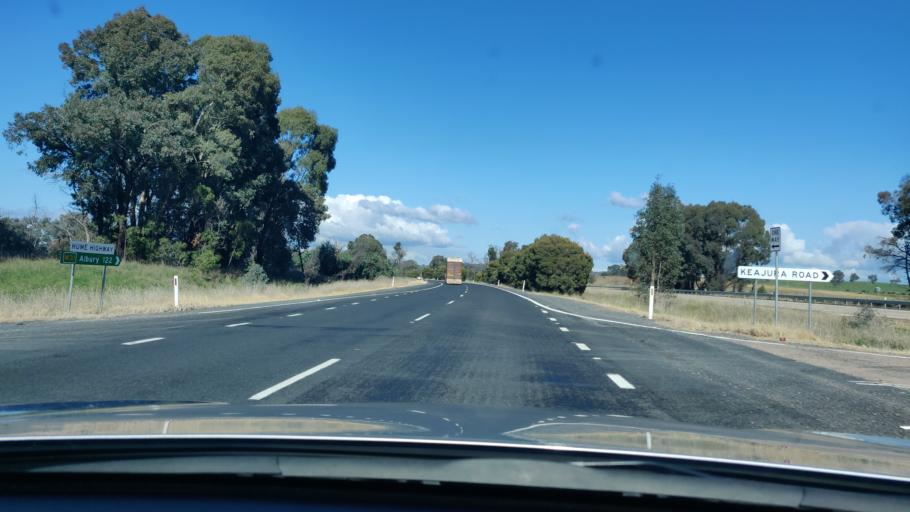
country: AU
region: New South Wales
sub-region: Wagga Wagga
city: Forest Hill
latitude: -35.3265
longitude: 147.6465
